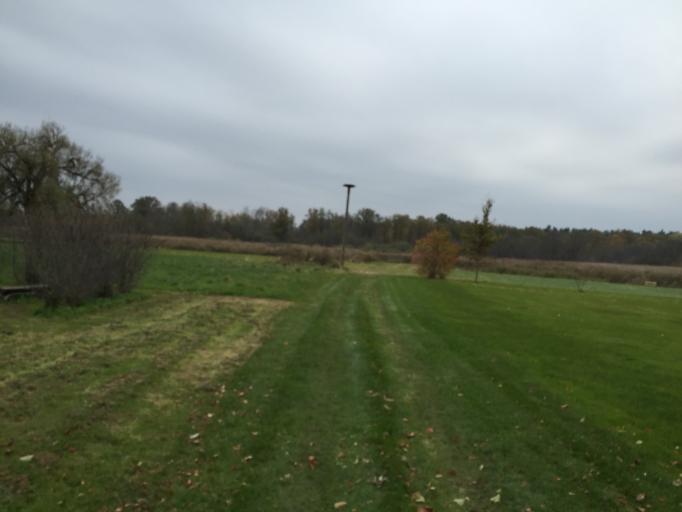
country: LV
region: Ozolnieku
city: Ozolnieki
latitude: 56.6386
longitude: 23.7781
